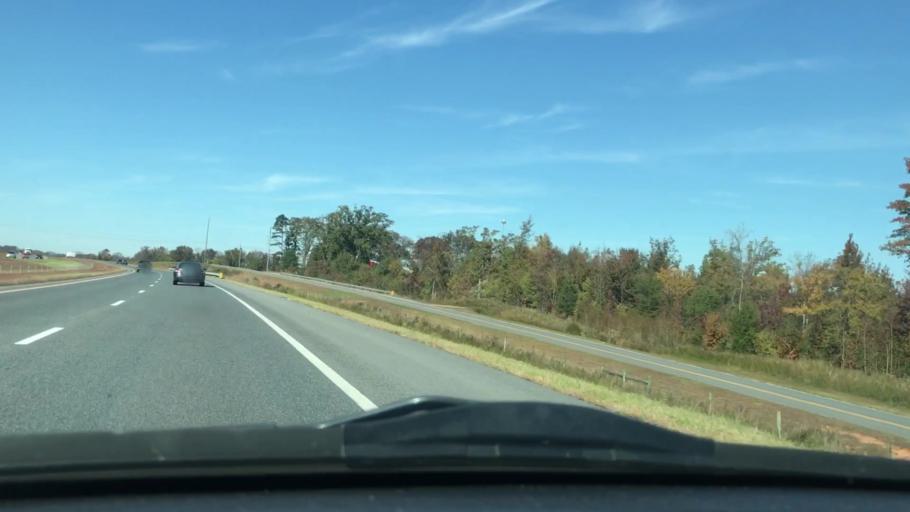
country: US
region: North Carolina
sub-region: Randolph County
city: Randleman
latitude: 35.8409
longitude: -79.8639
